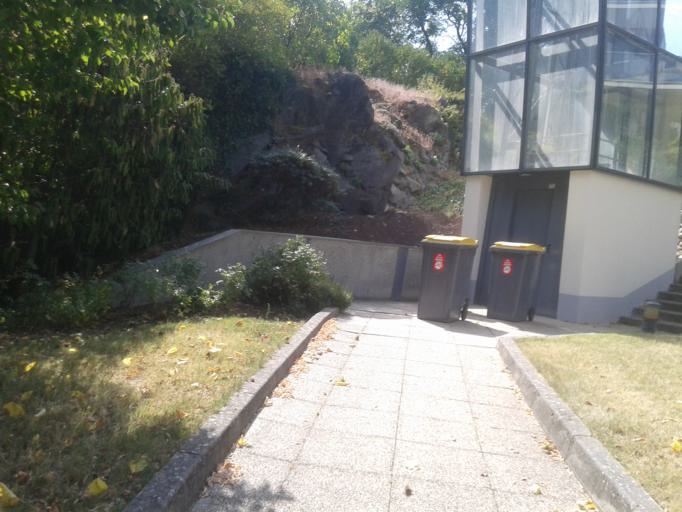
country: FR
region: Auvergne
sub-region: Departement du Puy-de-Dome
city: Chamalieres
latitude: 45.7768
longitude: 3.0588
